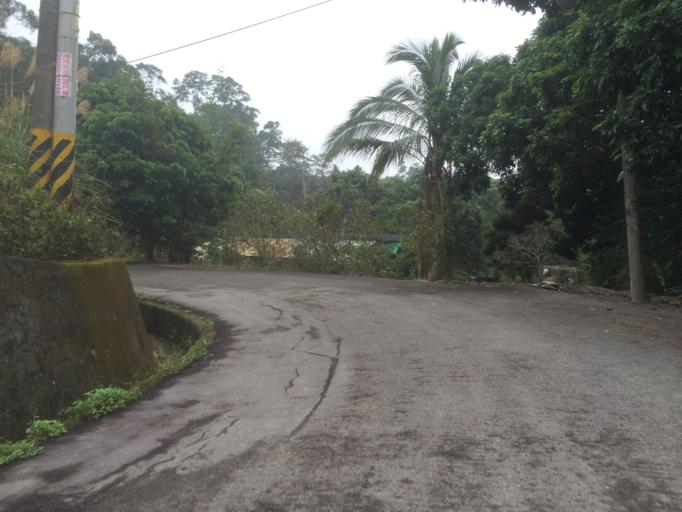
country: TW
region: Taiwan
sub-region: Taichung City
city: Taichung
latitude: 24.1705
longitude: 120.7859
